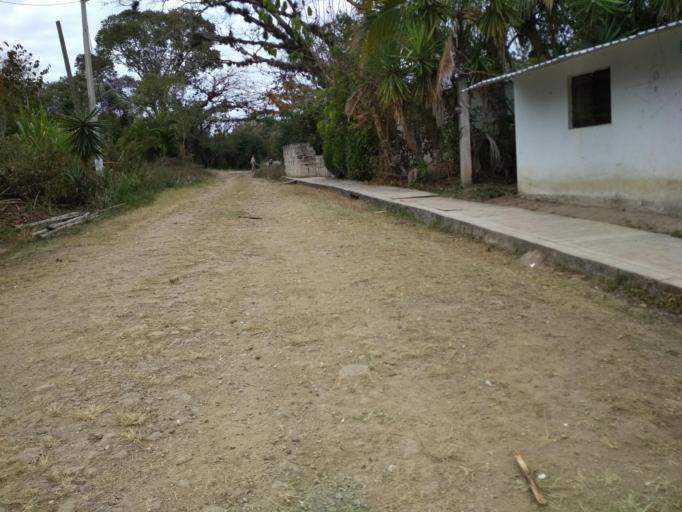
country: MX
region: Veracruz
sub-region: Coatepec
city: Tuzamapan
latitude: 19.3665
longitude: -96.8813
